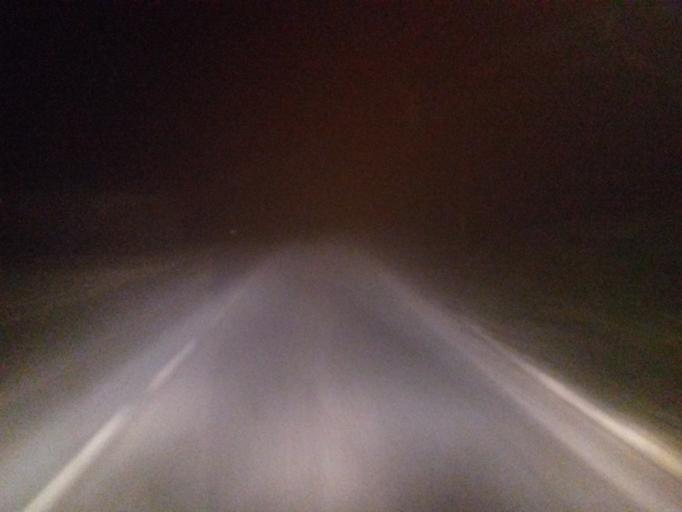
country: BA
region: Federation of Bosnia and Herzegovina
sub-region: Kanton Sarajevo
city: Sarajevo
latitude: 43.7908
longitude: 18.3608
